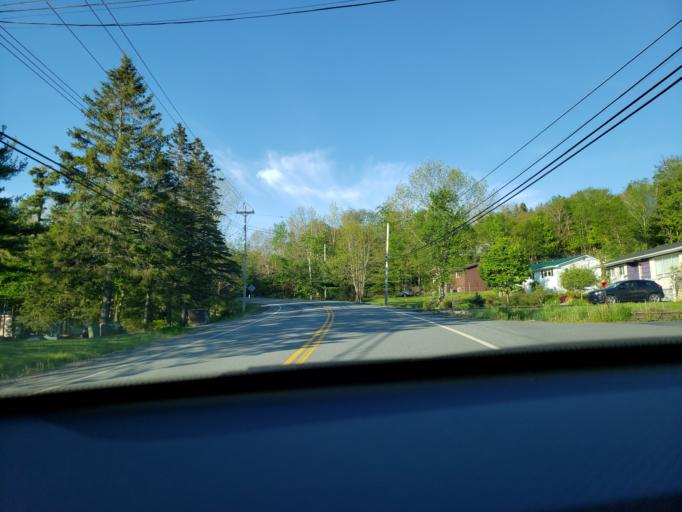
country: CA
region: Nova Scotia
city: Cole Harbour
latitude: 44.7331
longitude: -63.3926
